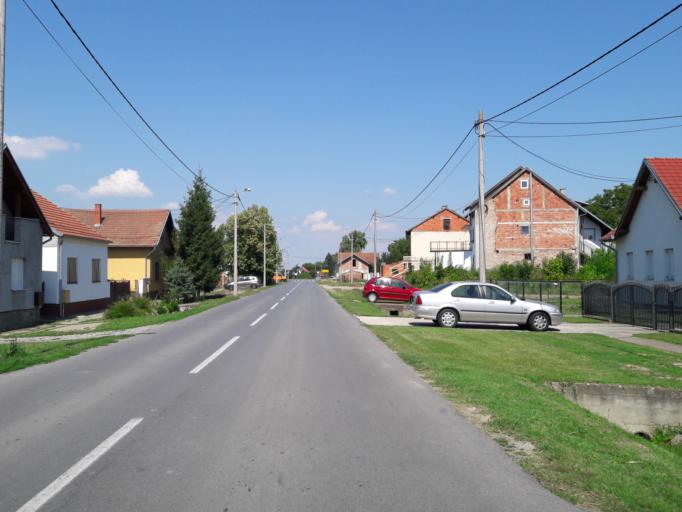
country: HR
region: Osjecko-Baranjska
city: Ernestinovo
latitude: 45.4444
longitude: 18.6621
